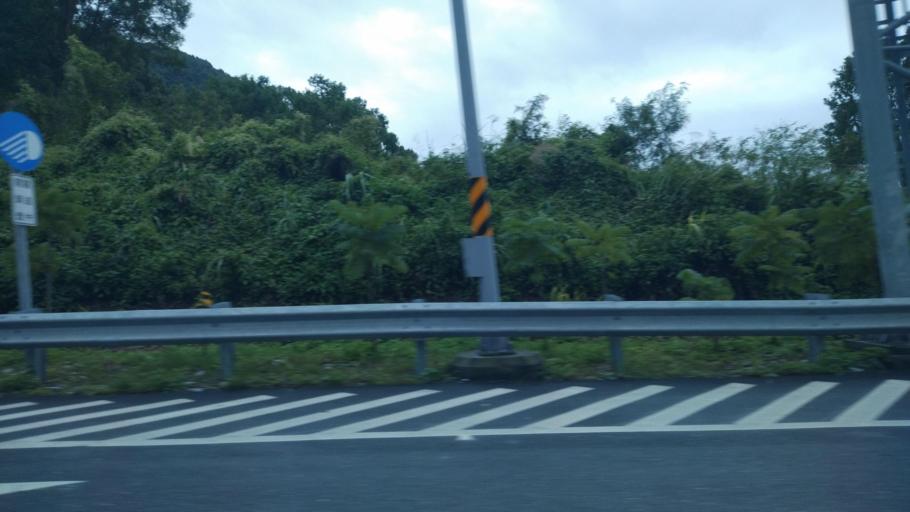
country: TW
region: Taiwan
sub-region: Hualien
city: Hualian
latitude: 24.2481
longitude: 121.7151
